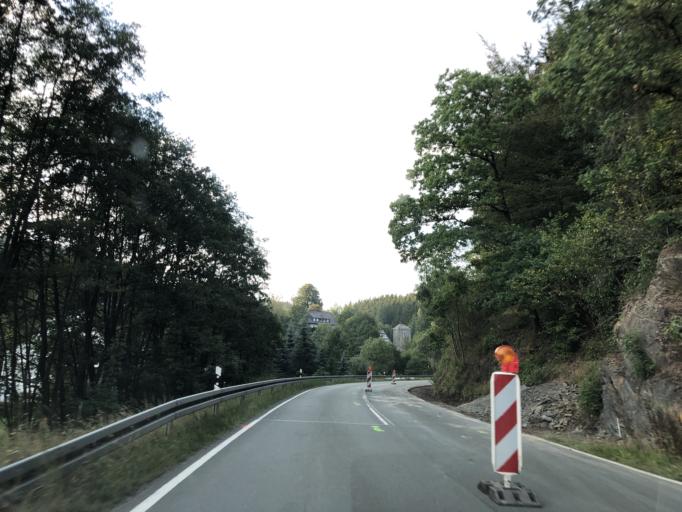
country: DE
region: North Rhine-Westphalia
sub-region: Regierungsbezirk Arnsberg
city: Winterberg
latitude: 51.1569
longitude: 8.5577
